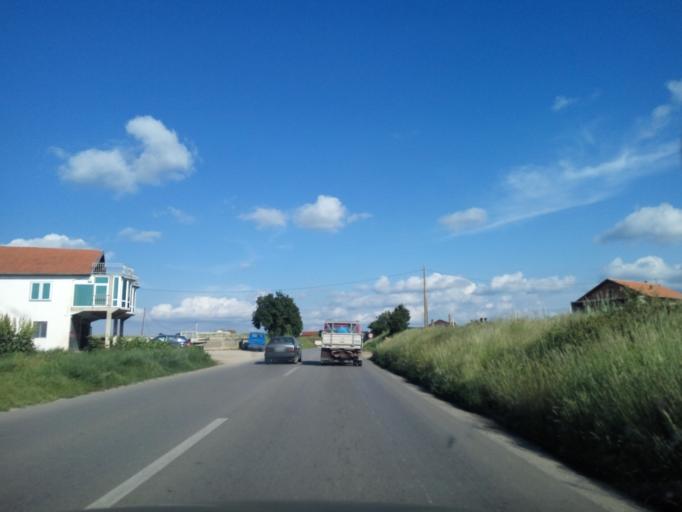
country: XK
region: Pec
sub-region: Komuna e Klines
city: Klina
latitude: 42.5935
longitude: 20.6602
